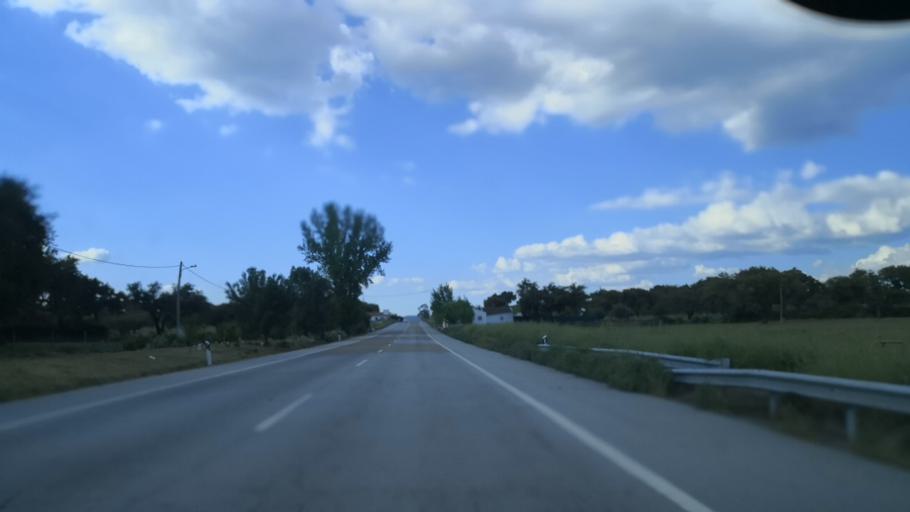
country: PT
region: Portalegre
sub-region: Portalegre
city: Urra
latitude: 39.2339
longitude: -7.4533
